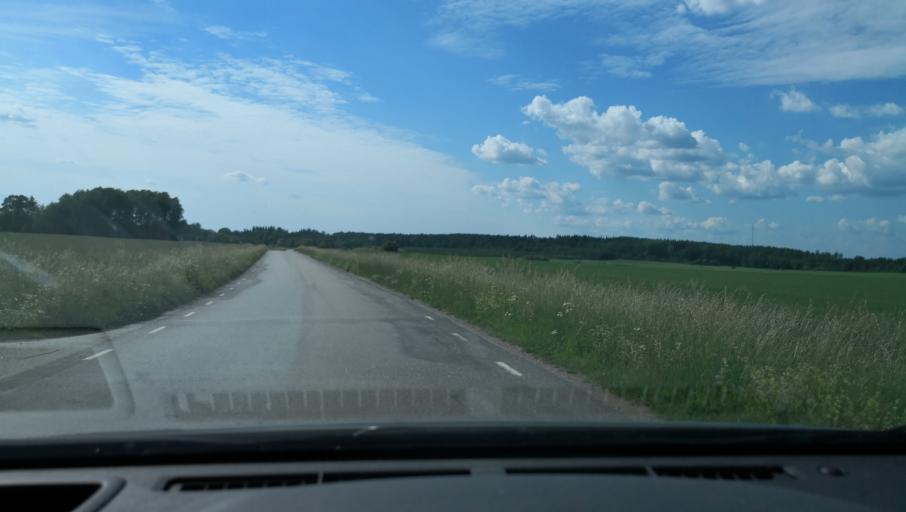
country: SE
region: Uppsala
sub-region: Enkopings Kommun
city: Orsundsbro
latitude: 59.8130
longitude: 17.3818
